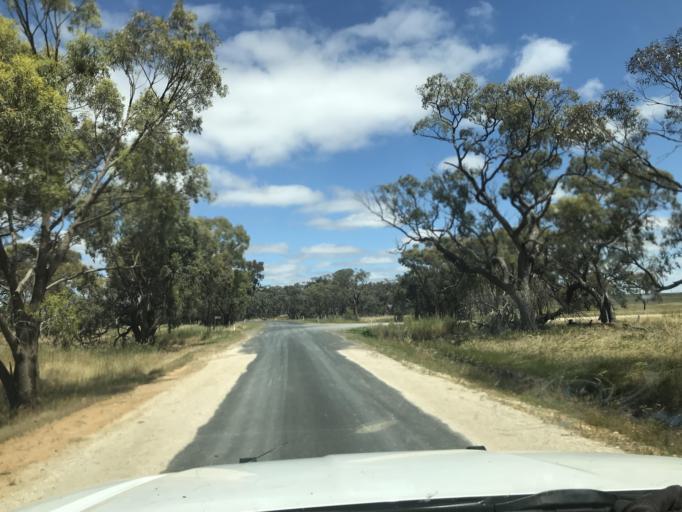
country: AU
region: South Australia
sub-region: Tatiara
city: Bordertown
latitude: -36.3085
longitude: 141.0421
